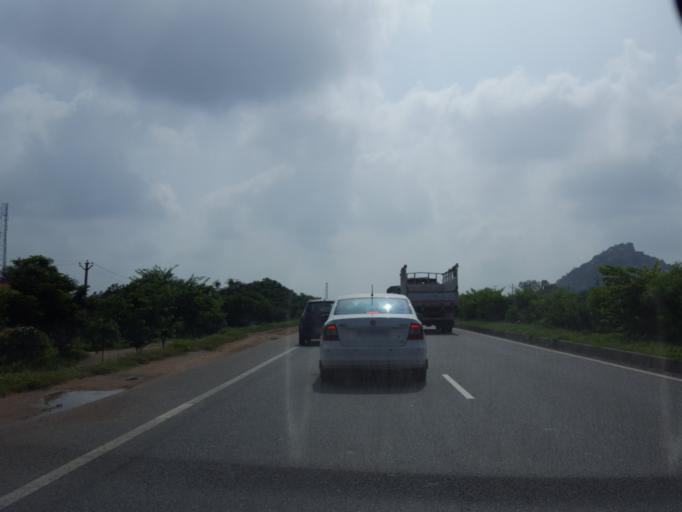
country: IN
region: Telangana
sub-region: Nalgonda
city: Gudur
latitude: 17.2752
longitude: 78.8133
